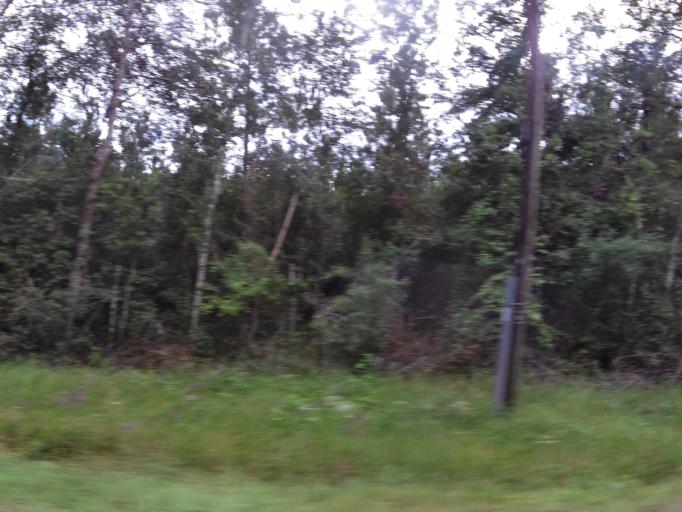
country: US
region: Florida
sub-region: Duval County
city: Baldwin
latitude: 30.3915
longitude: -81.9394
